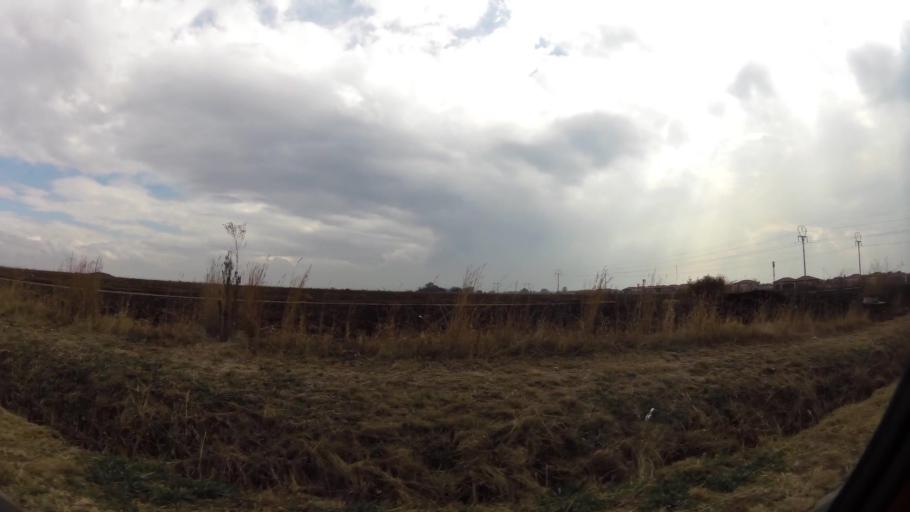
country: ZA
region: Gauteng
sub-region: Sedibeng District Municipality
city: Vanderbijlpark
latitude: -26.7195
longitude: 27.8836
